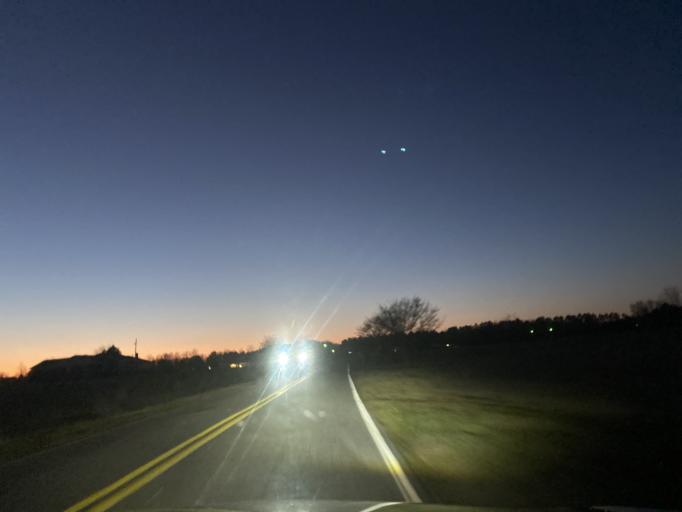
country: US
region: South Carolina
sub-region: Cherokee County
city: Gaffney
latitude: 35.1356
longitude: -81.7170
